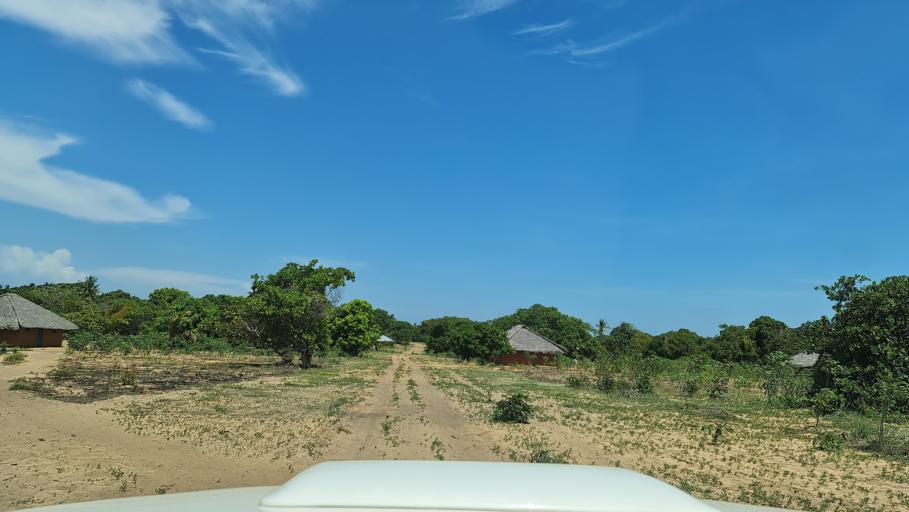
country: MZ
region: Nampula
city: Ilha de Mocambique
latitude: -15.1981
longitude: 40.6065
